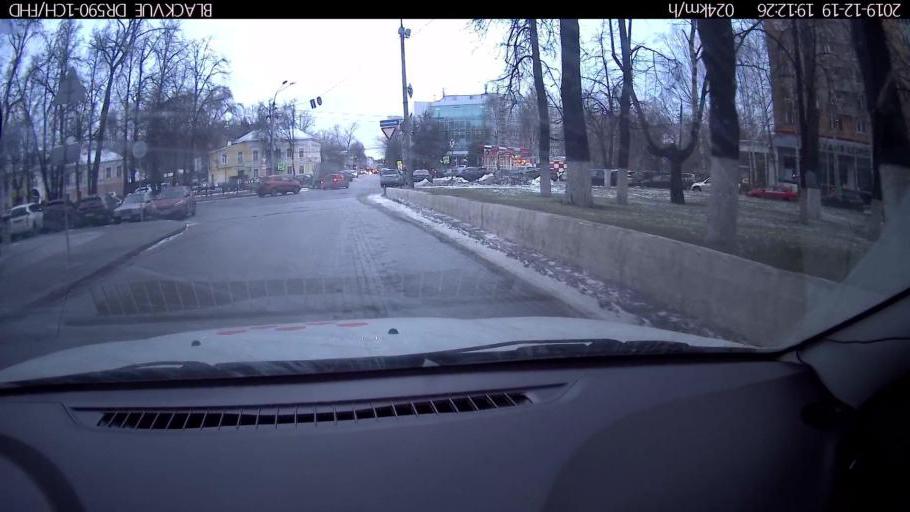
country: RU
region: Nizjnij Novgorod
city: Nizhniy Novgorod
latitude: 56.3167
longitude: 44.0018
